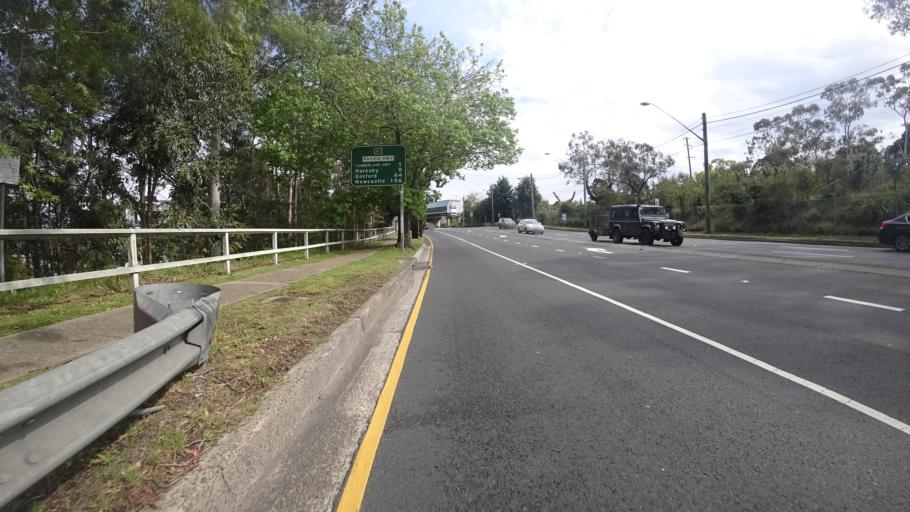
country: AU
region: New South Wales
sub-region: City of Sydney
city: Pymble
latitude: -33.7464
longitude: 151.1447
